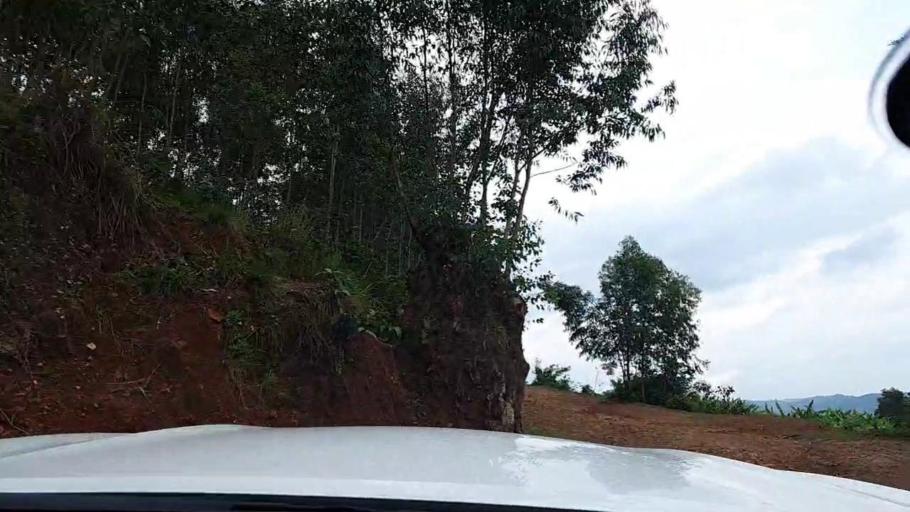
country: RW
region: Western Province
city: Kibuye
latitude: -2.1892
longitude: 29.3005
